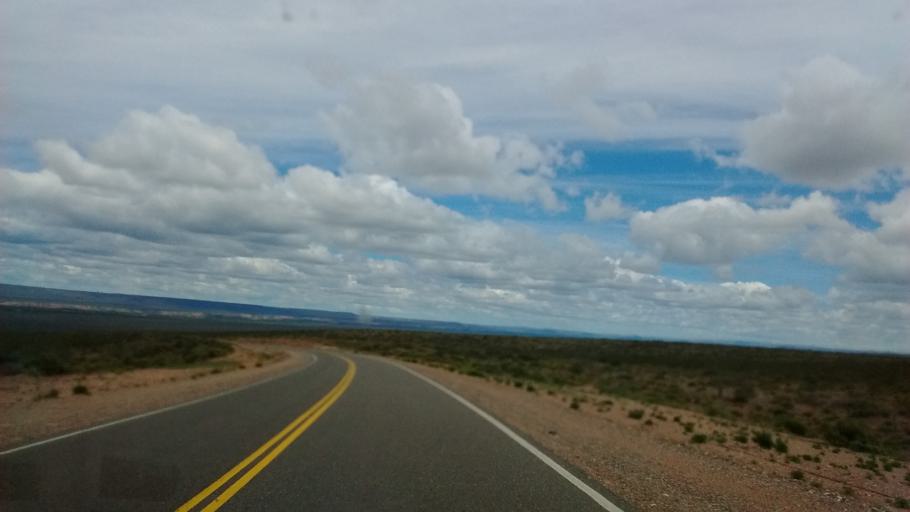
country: AR
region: Neuquen
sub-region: Departamento de Picun Leufu
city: Picun Leufu
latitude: -39.7607
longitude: -69.6481
